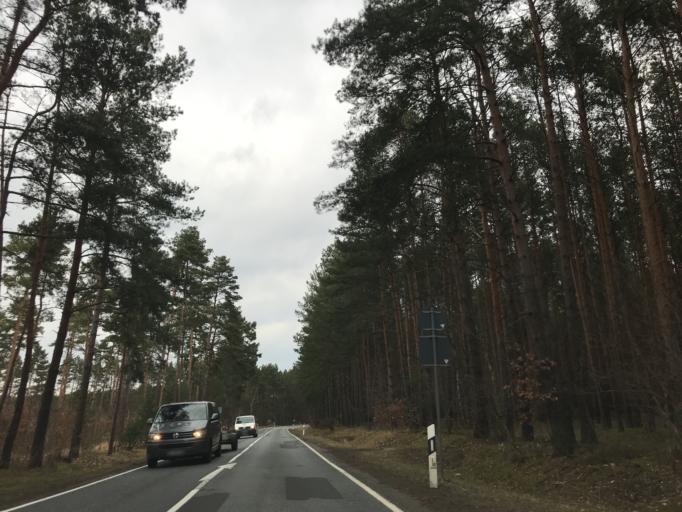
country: DE
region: Brandenburg
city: Fichtenwalde
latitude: 52.2978
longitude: 12.8616
